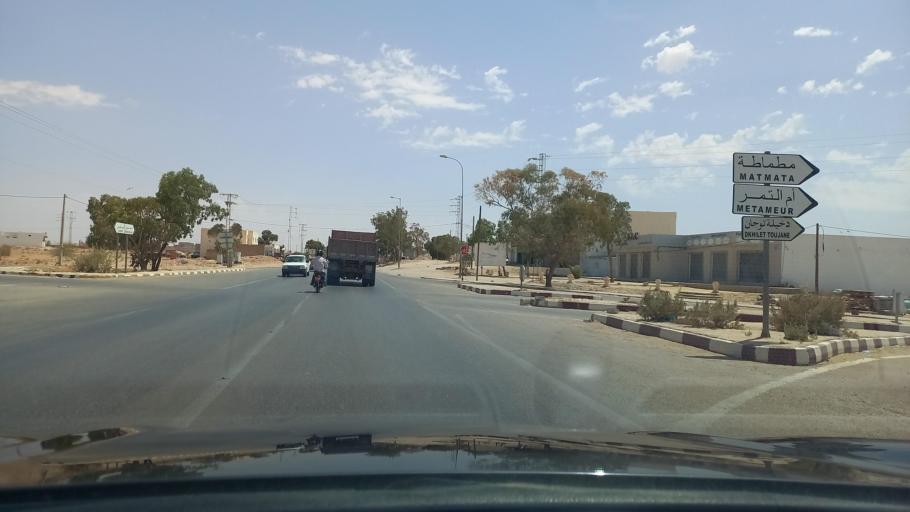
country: TN
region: Madanin
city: Medenine
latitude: 33.3726
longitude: 10.4471
